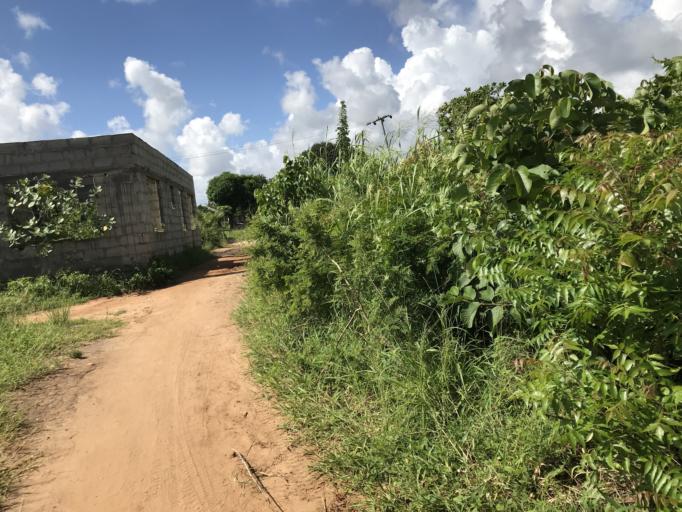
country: TZ
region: Dar es Salaam
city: Dar es Salaam
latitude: -6.8830
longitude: 39.4383
